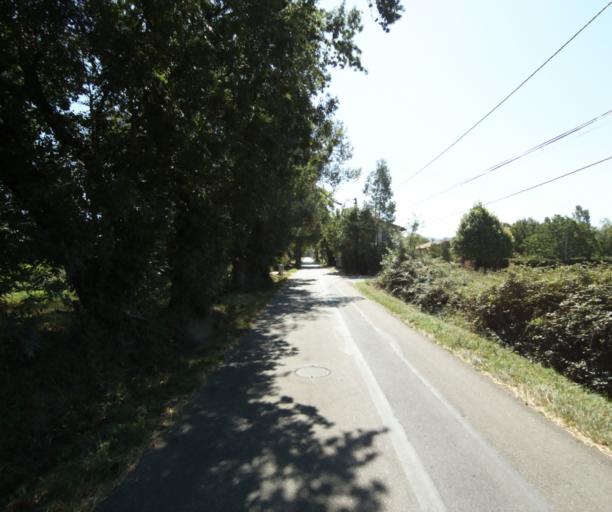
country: FR
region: Midi-Pyrenees
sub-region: Departement de la Haute-Garonne
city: Revel
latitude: 43.4685
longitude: 2.0004
